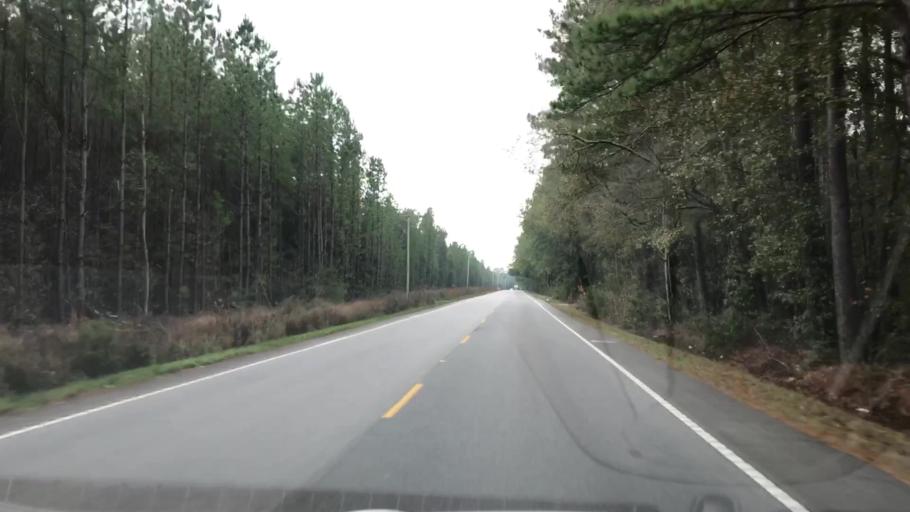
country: US
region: South Carolina
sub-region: Jasper County
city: Ridgeland
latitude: 32.5040
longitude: -80.8868
